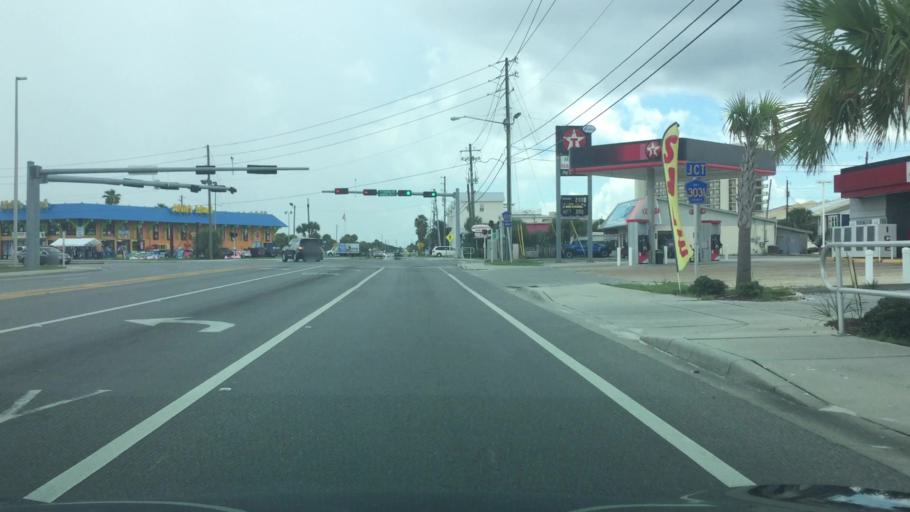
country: US
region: Florida
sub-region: Bay County
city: Lower Grand Lagoon
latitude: 30.1397
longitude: -85.7511
